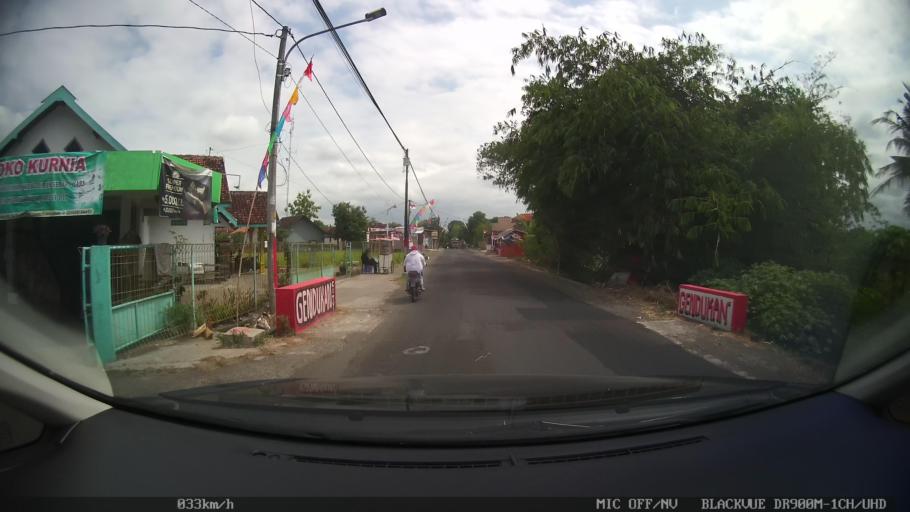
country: ID
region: Central Java
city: Candi Prambanan
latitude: -7.7782
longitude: 110.4749
